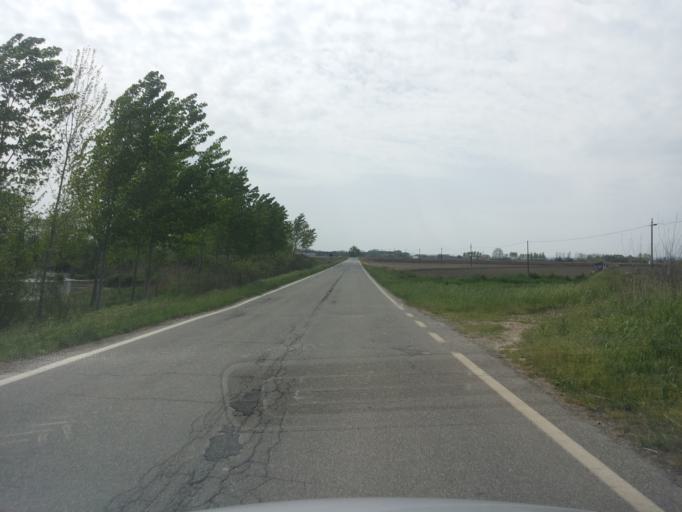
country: IT
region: Piedmont
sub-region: Provincia di Vercelli
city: Motta De Conti
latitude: 45.2044
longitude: 8.5156
